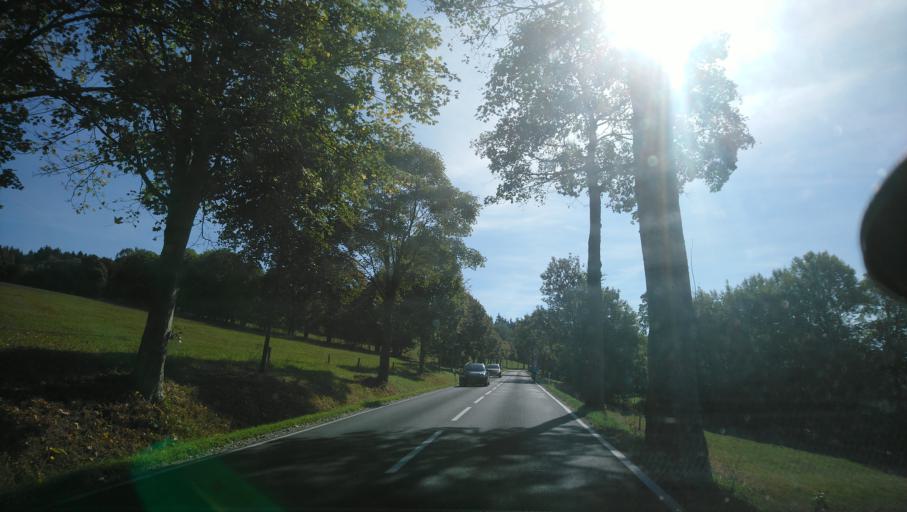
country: DE
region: Saxony
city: Konigswalde
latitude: 50.5340
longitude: 13.0593
